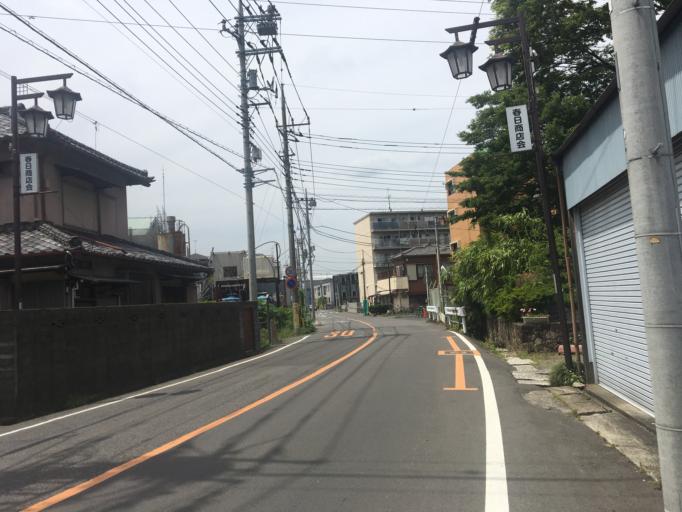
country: JP
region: Saitama
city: Shimotoda
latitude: 35.8326
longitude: 139.6680
